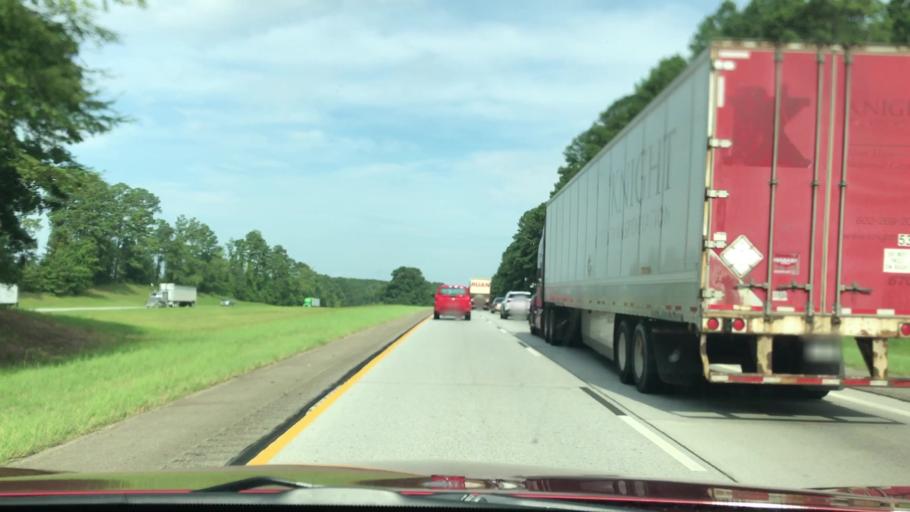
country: US
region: Georgia
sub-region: Columbia County
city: Appling
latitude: 33.5027
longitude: -82.3645
